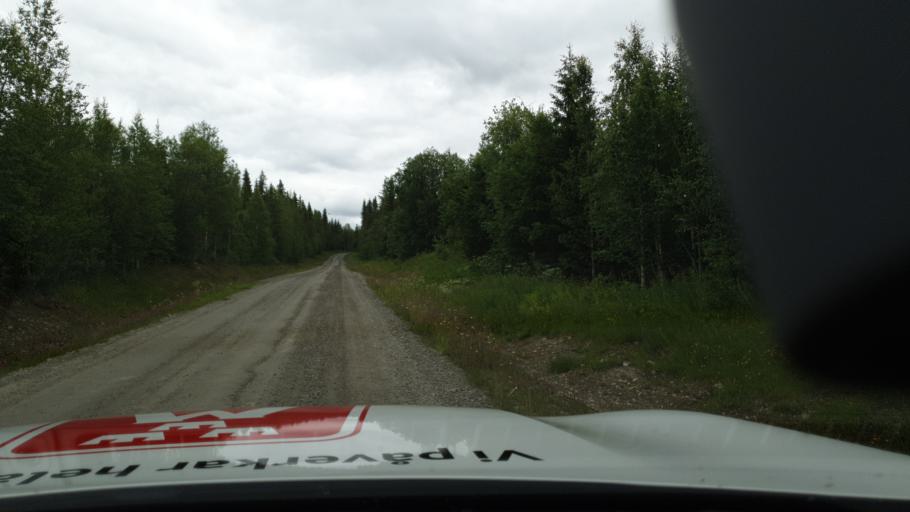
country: SE
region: Vaesterbotten
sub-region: Storumans Kommun
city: Storuman
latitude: 64.7873
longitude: 17.0209
